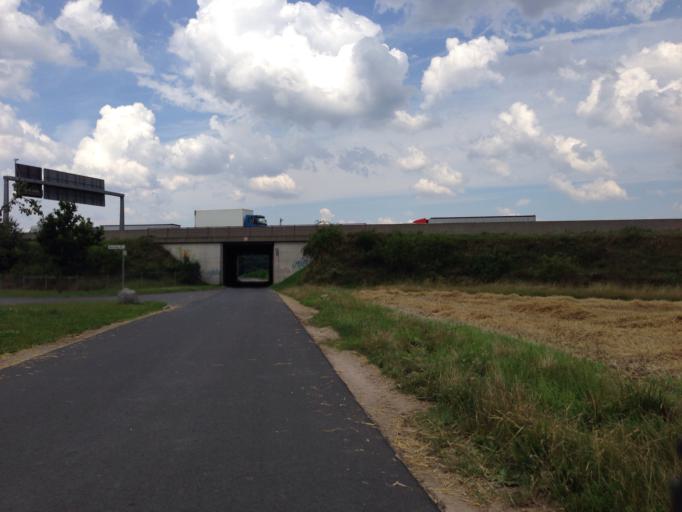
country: DE
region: Hesse
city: Obertshausen
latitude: 50.0591
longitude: 8.8760
